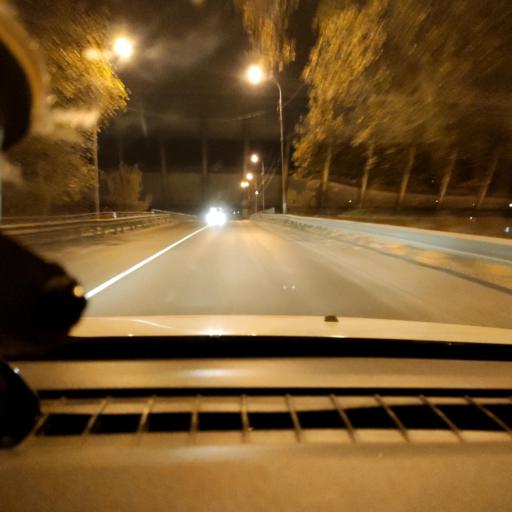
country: RU
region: Samara
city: Rozhdestveno
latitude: 53.1516
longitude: 50.0676
